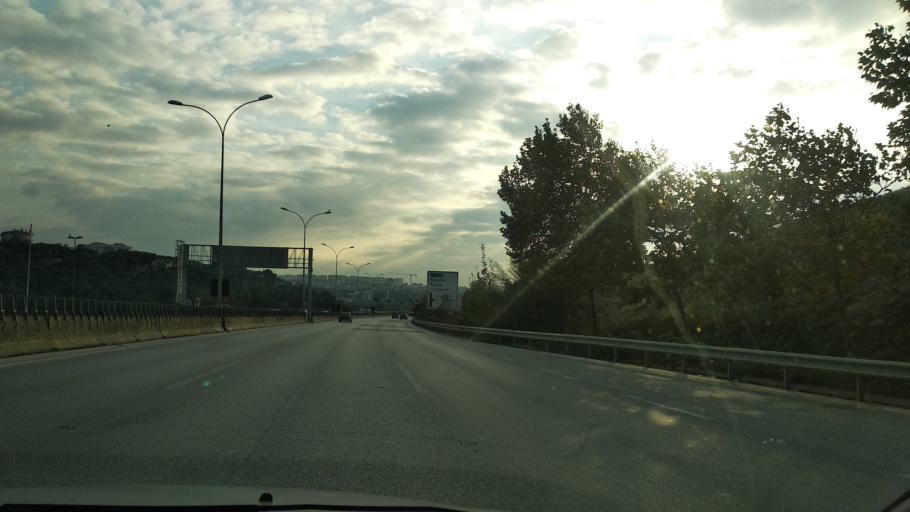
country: TR
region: Istanbul
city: Icmeler
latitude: 40.8862
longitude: 29.3230
